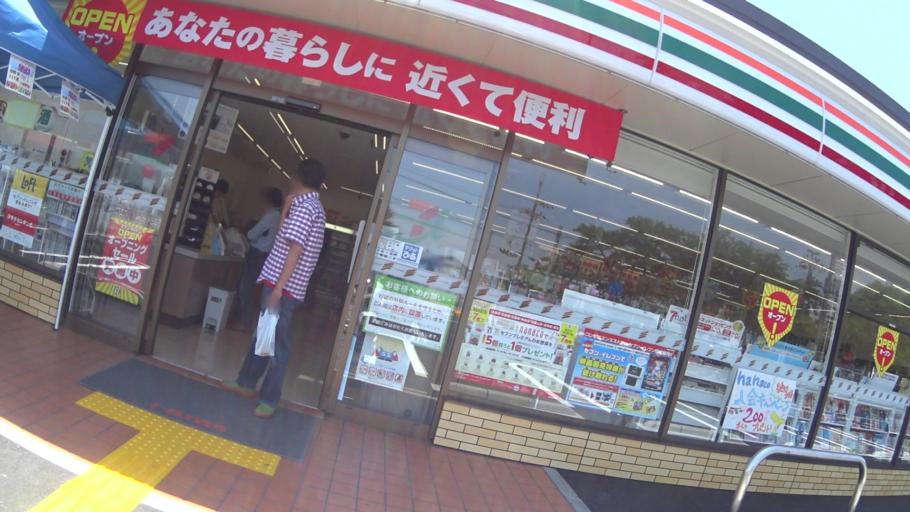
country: JP
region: Kyoto
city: Ayabe
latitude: 35.1754
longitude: 135.4077
